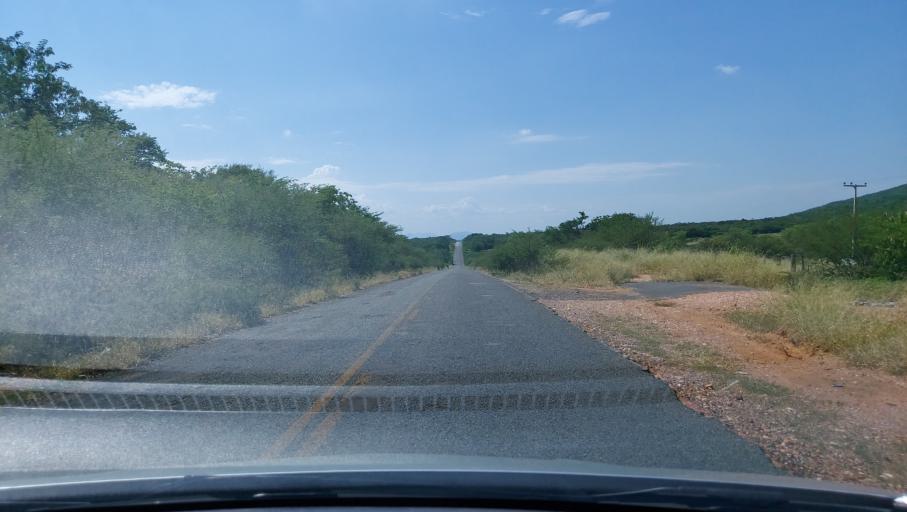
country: BR
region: Bahia
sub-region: Oliveira Dos Brejinhos
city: Beira Rio
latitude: -12.1709
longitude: -42.5458
